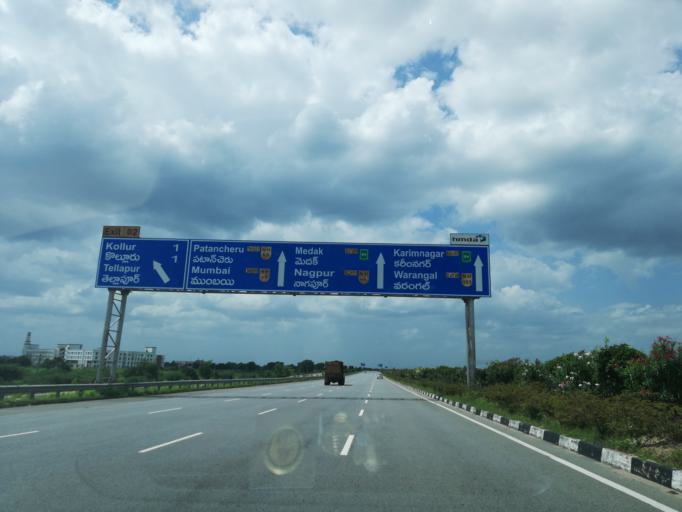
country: IN
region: Telangana
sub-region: Medak
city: Serilingampalle
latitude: 17.4497
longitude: 78.2547
